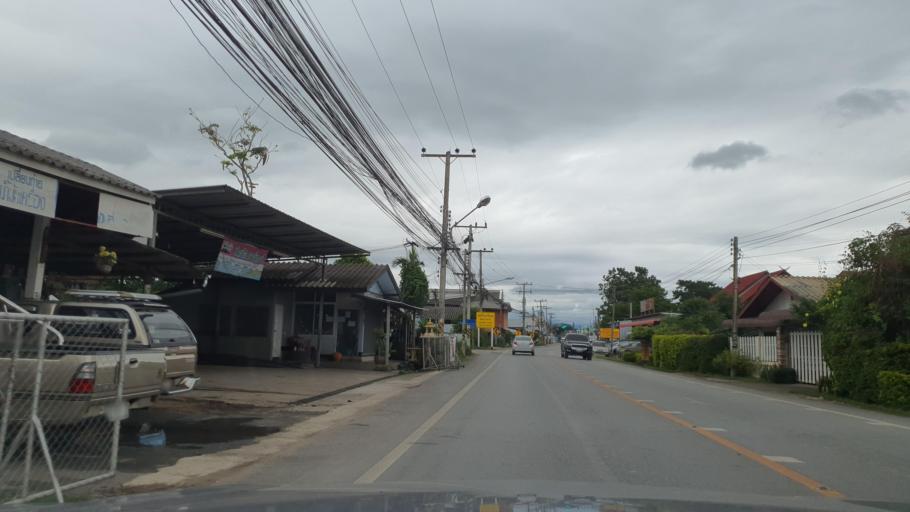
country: TH
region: Chiang Mai
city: San Pa Tong
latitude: 18.6150
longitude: 98.9542
